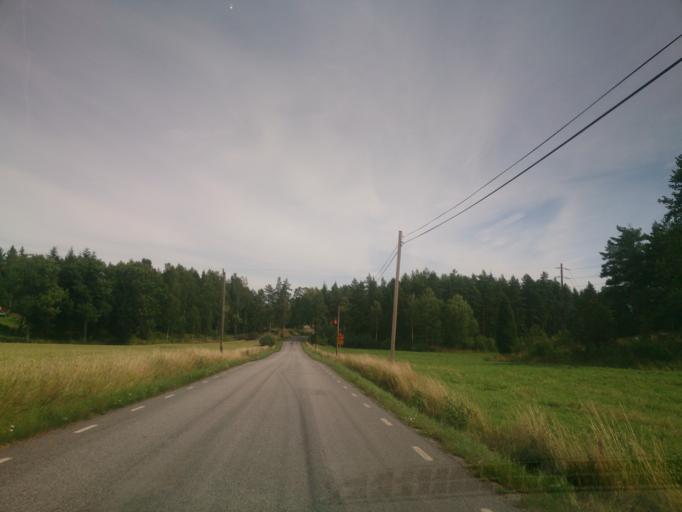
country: SE
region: OEstergoetland
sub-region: Valdemarsviks Kommun
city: Gusum
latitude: 58.3234
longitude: 16.3860
